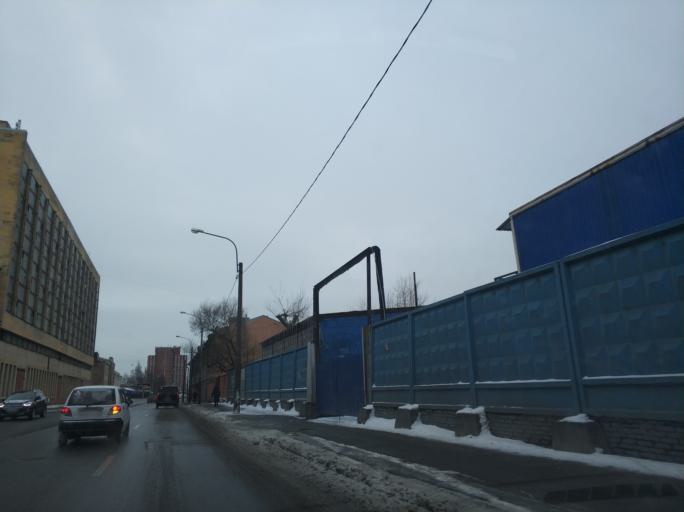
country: RU
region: St.-Petersburg
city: Centralniy
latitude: 59.9190
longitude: 30.3738
